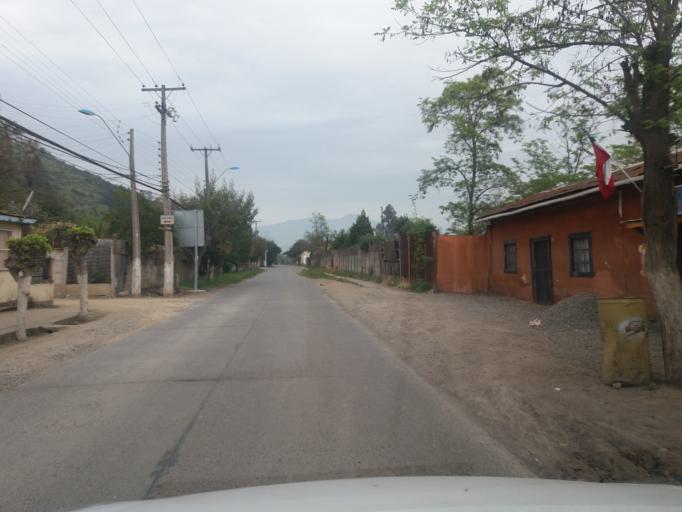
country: CL
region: Valparaiso
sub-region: Provincia de Quillota
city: Hacienda La Calera
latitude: -32.8223
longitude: -71.1314
